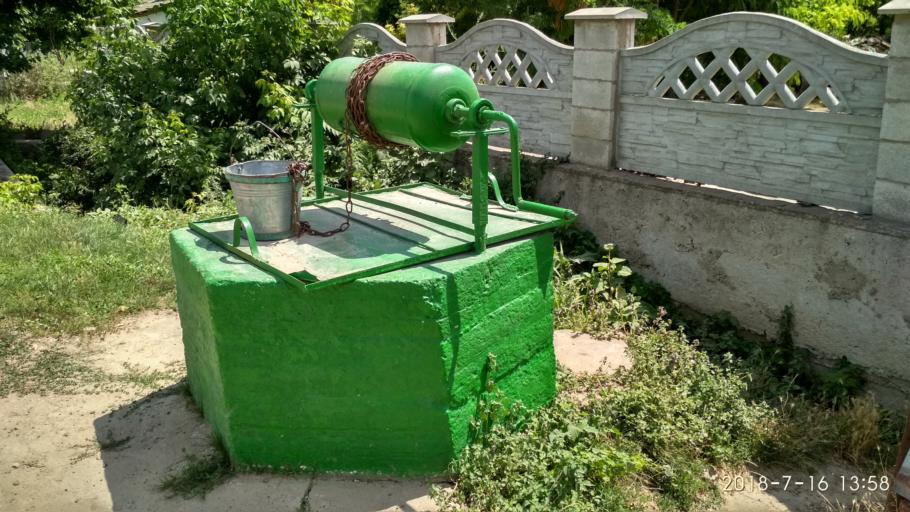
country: MD
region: Telenesti
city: Cocieri
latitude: 47.2237
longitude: 29.0604
